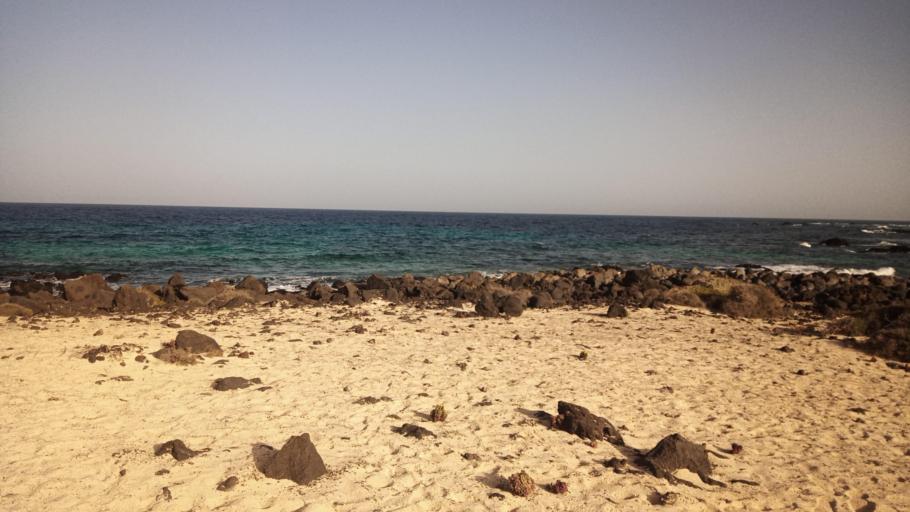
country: ES
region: Canary Islands
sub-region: Provincia de Las Palmas
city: Haria
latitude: 29.2064
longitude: -13.4245
